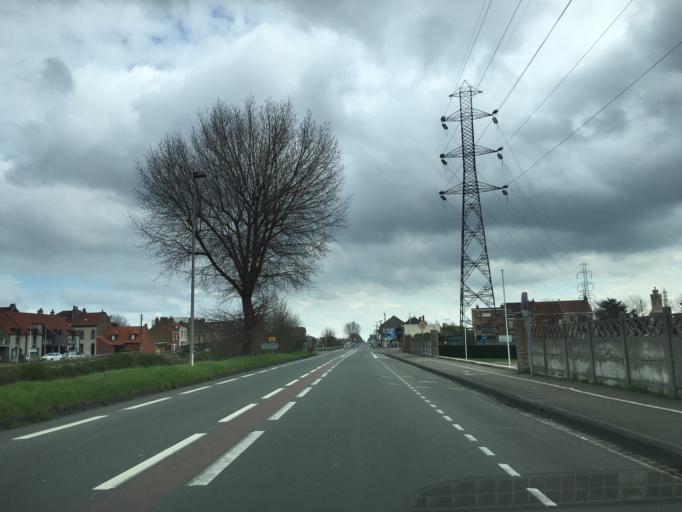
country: FR
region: Nord-Pas-de-Calais
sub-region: Departement du Nord
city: Coudekerque-Branche
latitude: 51.0305
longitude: 2.3890
